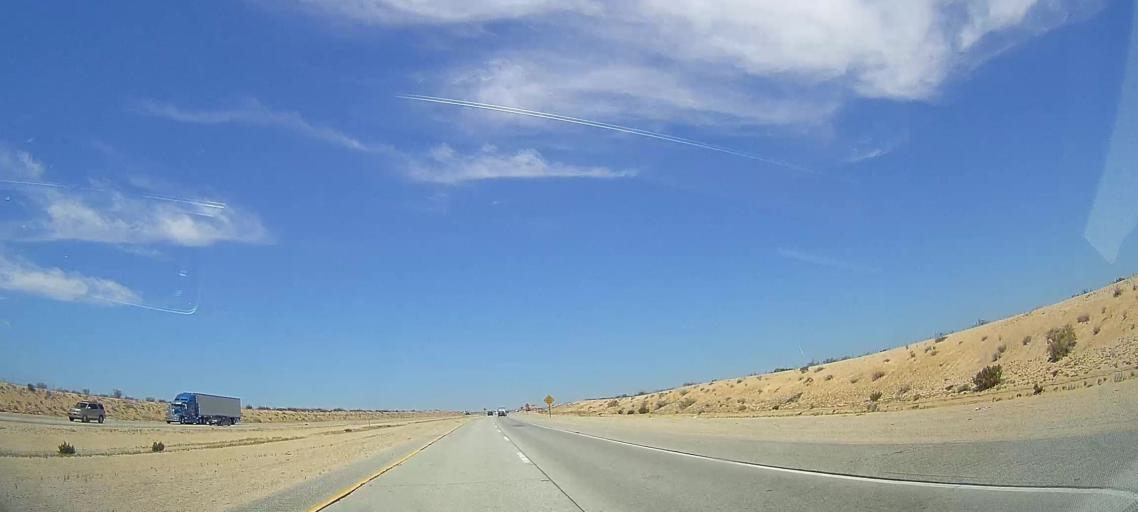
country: US
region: California
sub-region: Kern County
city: Boron
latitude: 34.9481
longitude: -117.4135
